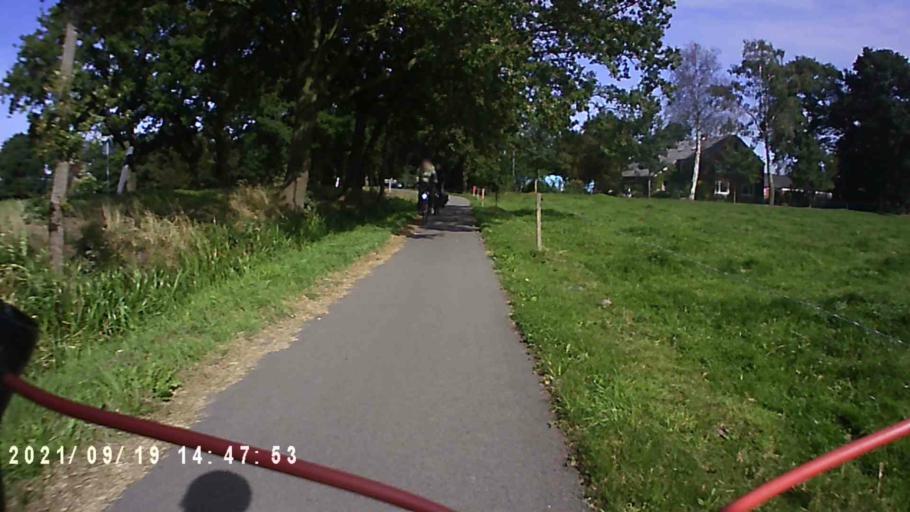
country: DE
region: Lower Saxony
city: Bunde
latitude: 53.1242
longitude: 7.1928
